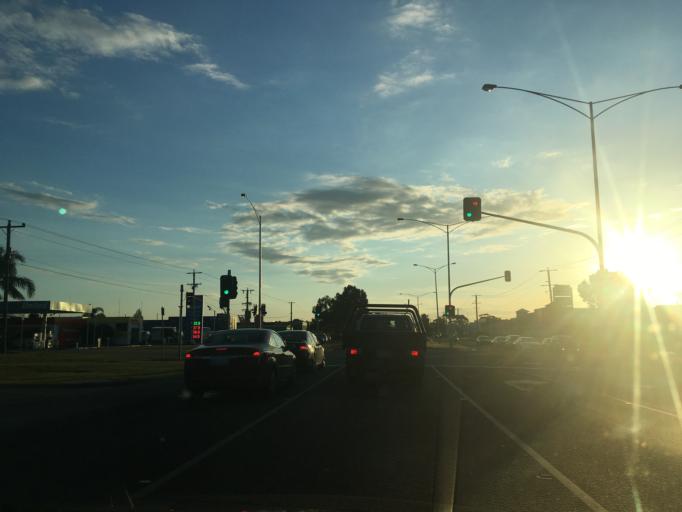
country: AU
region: Victoria
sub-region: Wyndham
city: Hoppers Crossing
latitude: -37.8766
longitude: 144.7140
